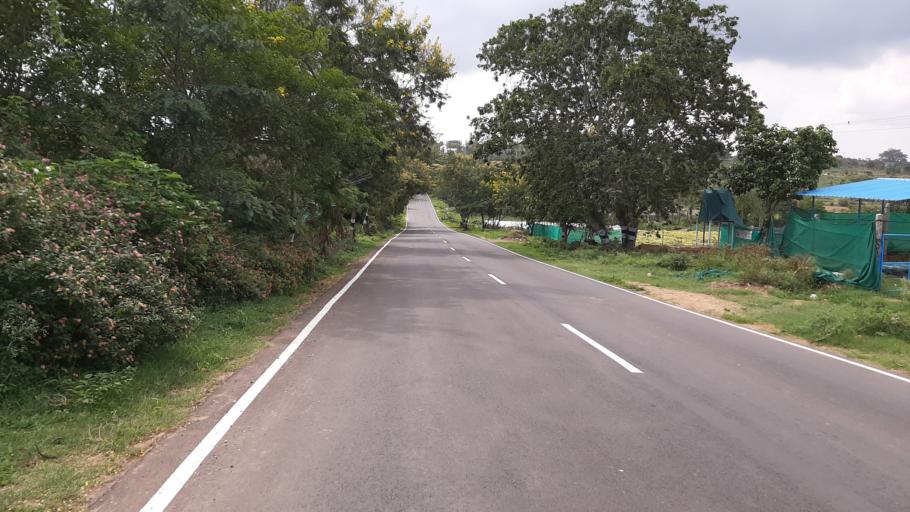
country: IN
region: Tamil Nadu
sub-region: Krishnagiri
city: Denkanikota
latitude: 12.5385
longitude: 77.7674
